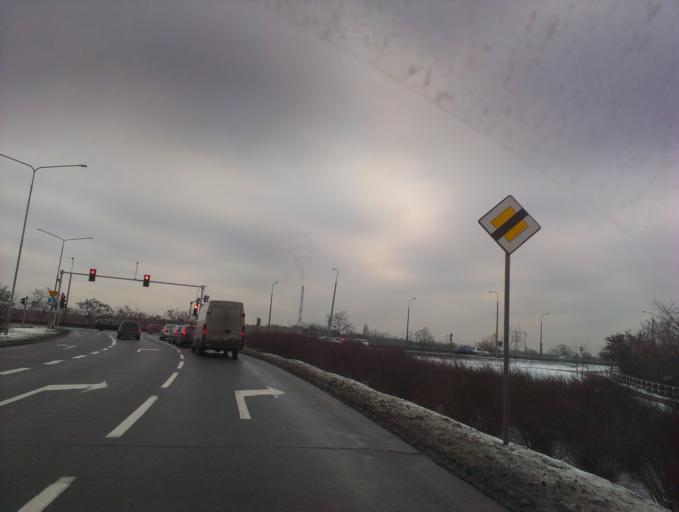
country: PL
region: Greater Poland Voivodeship
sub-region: Poznan
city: Poznan
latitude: 52.4304
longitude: 16.9602
